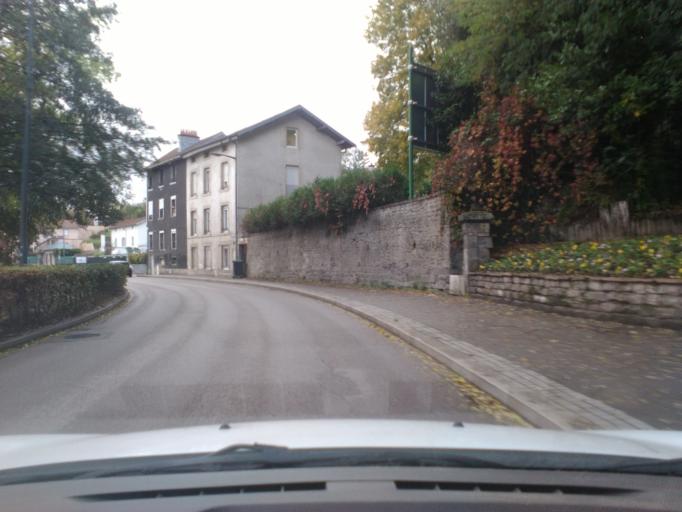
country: FR
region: Lorraine
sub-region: Departement des Vosges
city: Epinal
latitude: 48.1869
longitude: 6.4416
